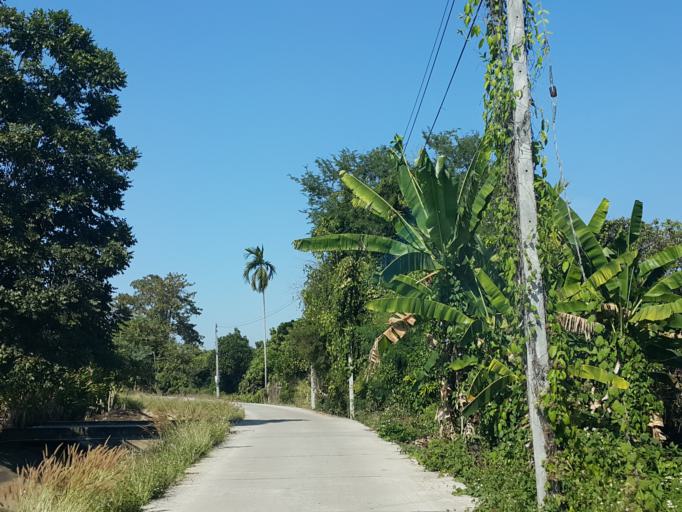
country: TH
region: Chiang Mai
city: San Sai
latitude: 18.8727
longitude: 98.9840
